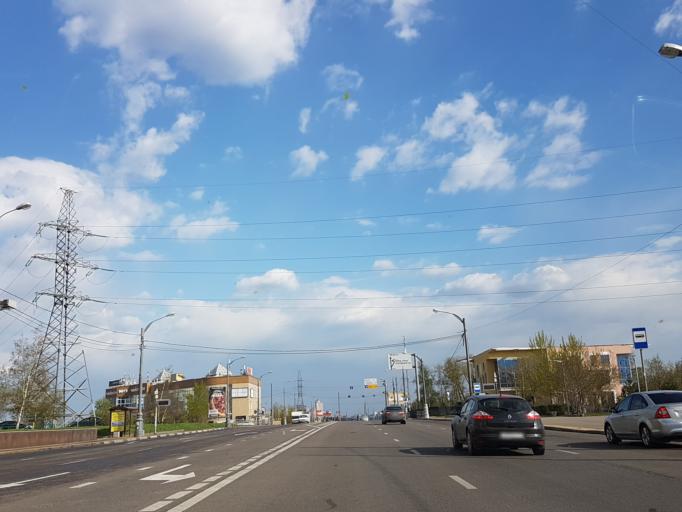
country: RU
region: Moscow
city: Strogino
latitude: 55.8372
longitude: 37.3816
